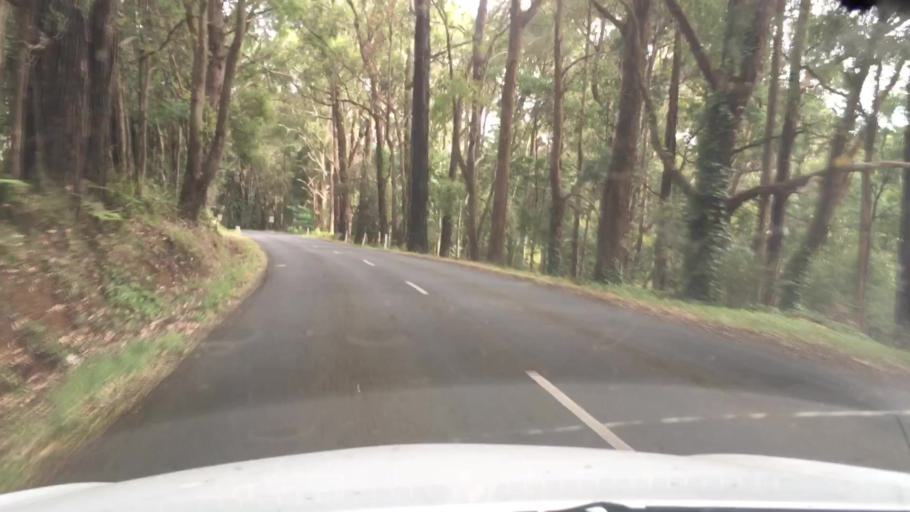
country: AU
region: Victoria
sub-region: Cardinia
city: Cockatoo
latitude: -37.9149
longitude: 145.4703
